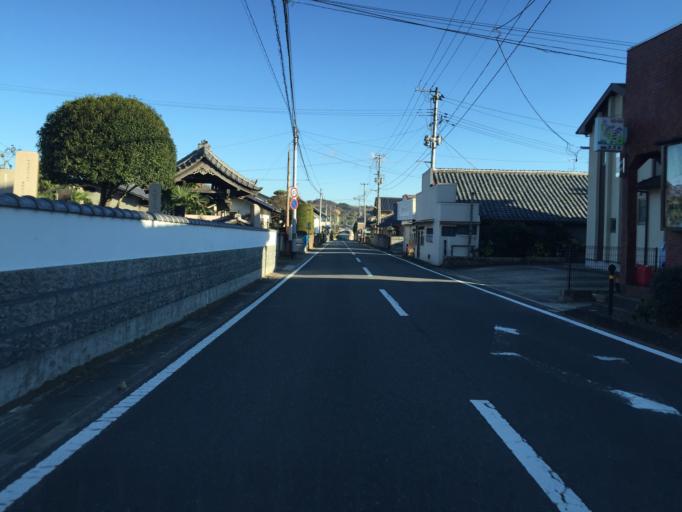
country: JP
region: Fukushima
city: Iwaki
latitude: 37.1352
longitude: 140.8561
